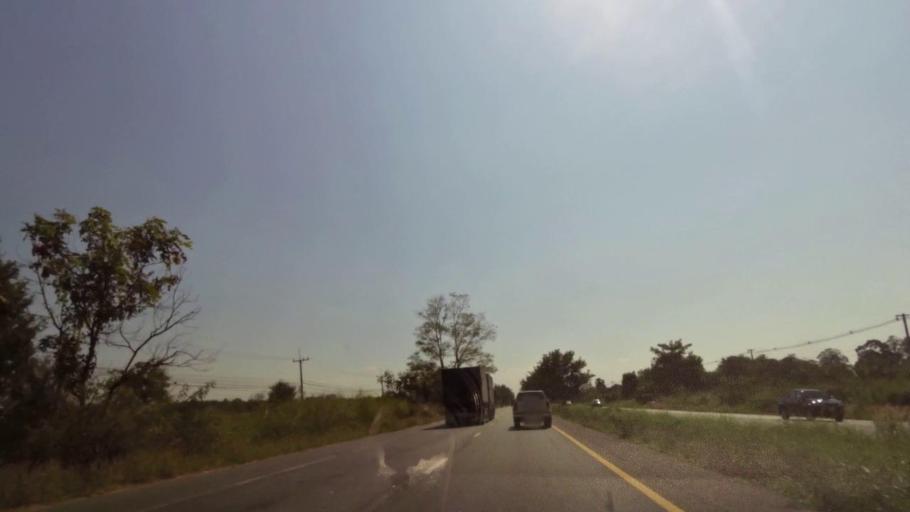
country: TH
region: Nakhon Sawan
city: Kao Liao
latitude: 15.8587
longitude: 100.1169
